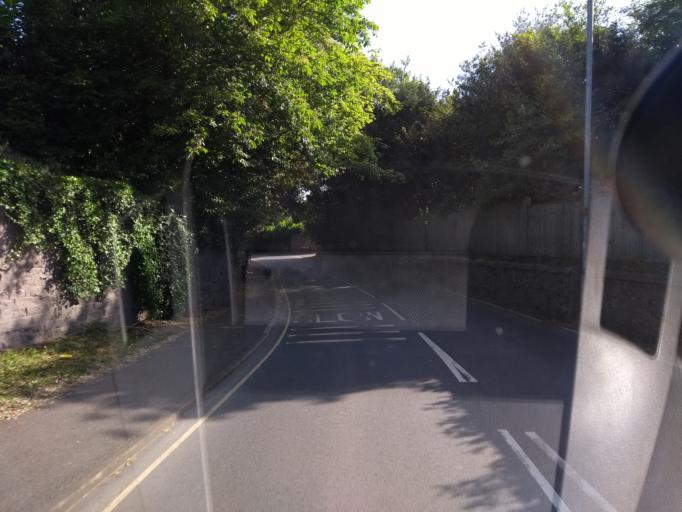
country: GB
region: England
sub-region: Somerset
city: Taunton
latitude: 51.0079
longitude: -3.1114
